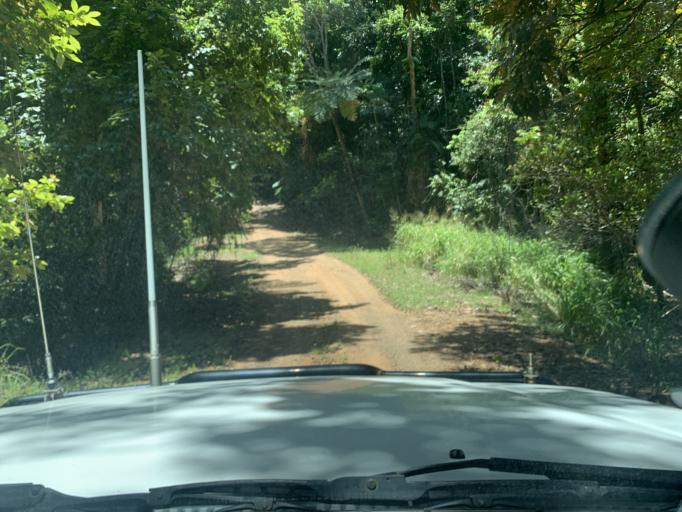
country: AU
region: Queensland
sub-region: Cairns
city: Woree
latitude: -16.9730
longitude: 145.6504
